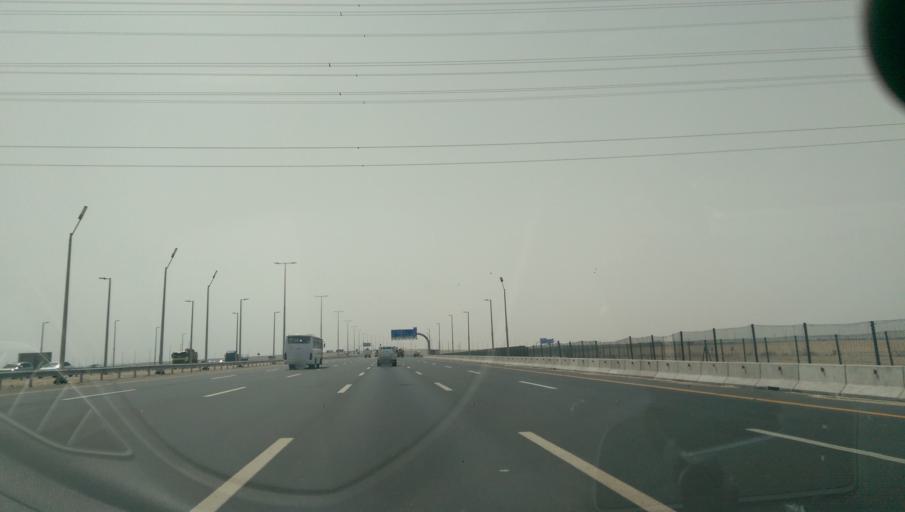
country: AE
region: Abu Dhabi
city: Abu Dhabi
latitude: 24.2955
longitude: 54.5439
